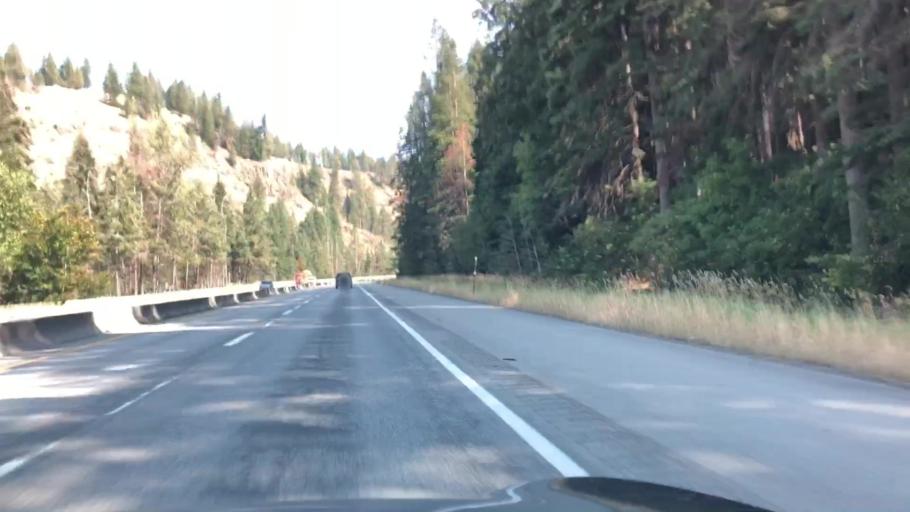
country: US
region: Idaho
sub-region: Kootenai County
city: Coeur d'Alene
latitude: 47.6305
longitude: -116.6061
